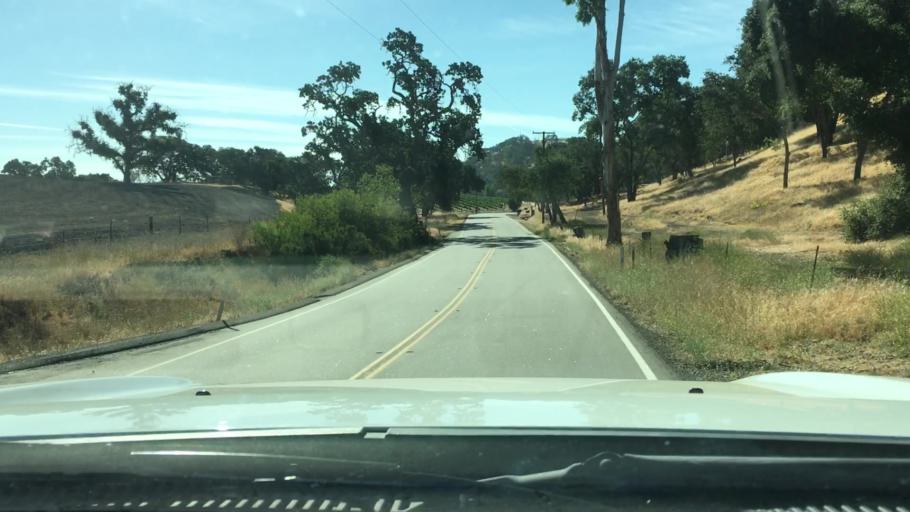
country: US
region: California
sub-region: San Luis Obispo County
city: Templeton
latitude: 35.5636
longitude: -120.6546
